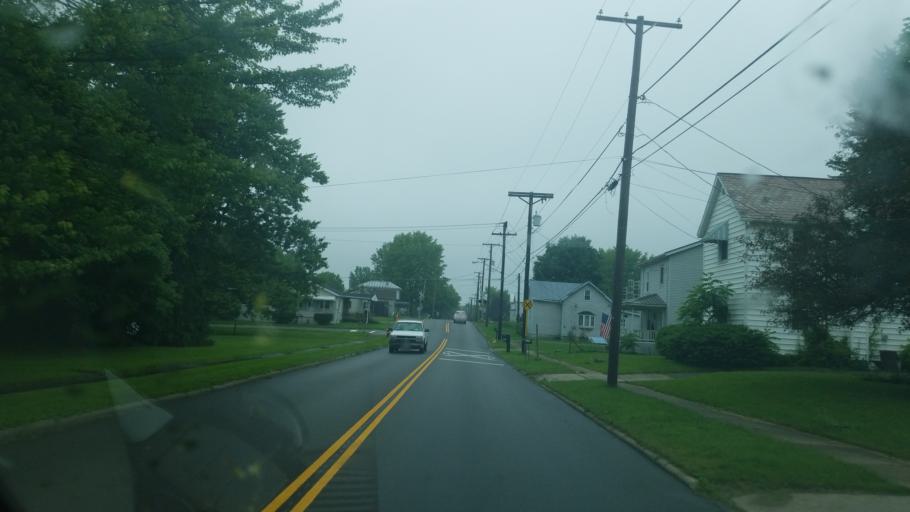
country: US
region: Ohio
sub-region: Crawford County
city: Bucyrus
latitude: 40.8061
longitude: -82.9591
